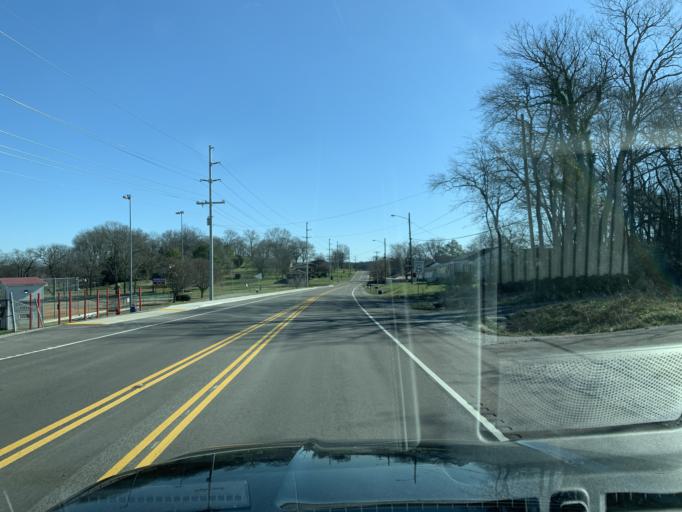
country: US
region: Tennessee
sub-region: Maury County
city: Mount Pleasant
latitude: 35.5429
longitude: -87.2180
